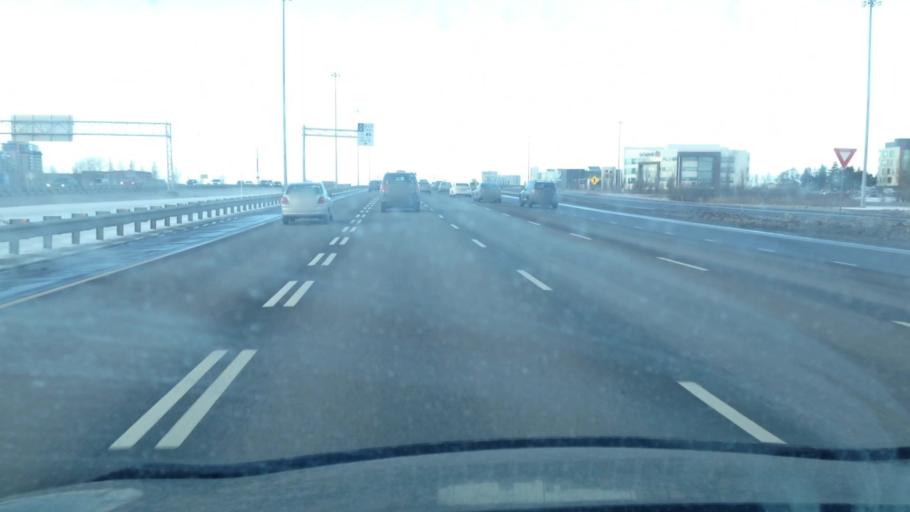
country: CA
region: Quebec
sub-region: Laval
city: Laval
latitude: 45.5608
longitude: -73.7343
